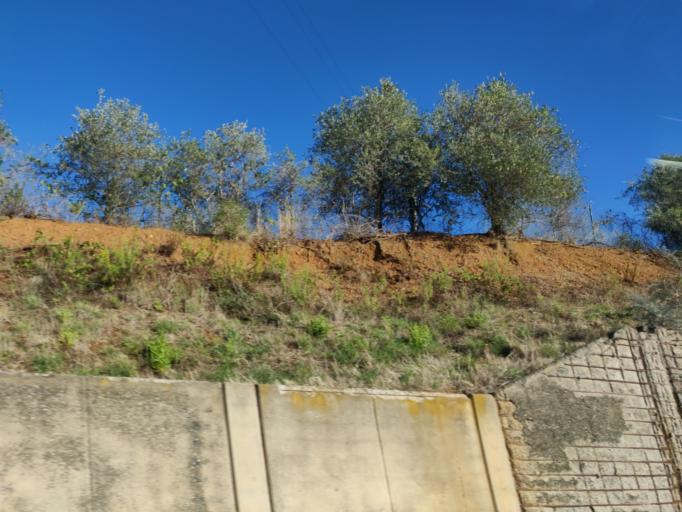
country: IT
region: Tuscany
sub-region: Provincia di Grosseto
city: Follonica
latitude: 42.9564
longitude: 10.7888
